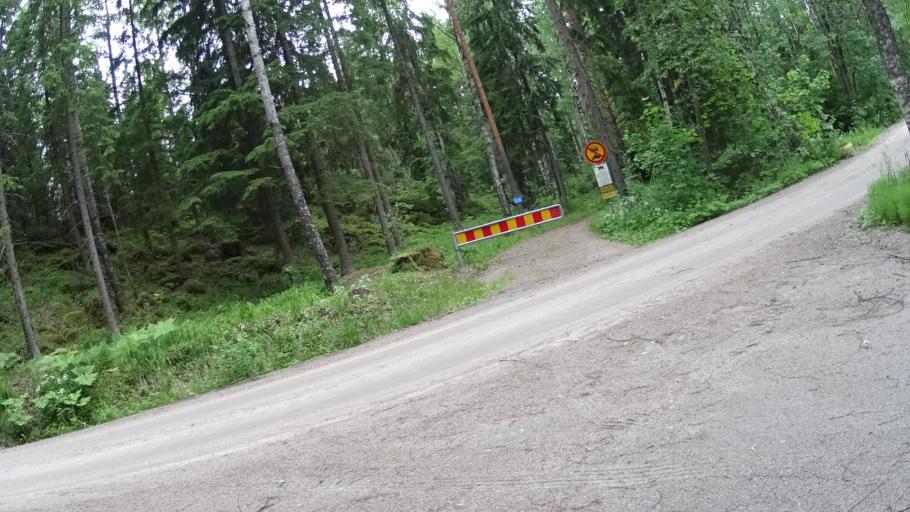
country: FI
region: Uusimaa
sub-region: Helsinki
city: Espoo
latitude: 60.2860
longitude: 24.5984
